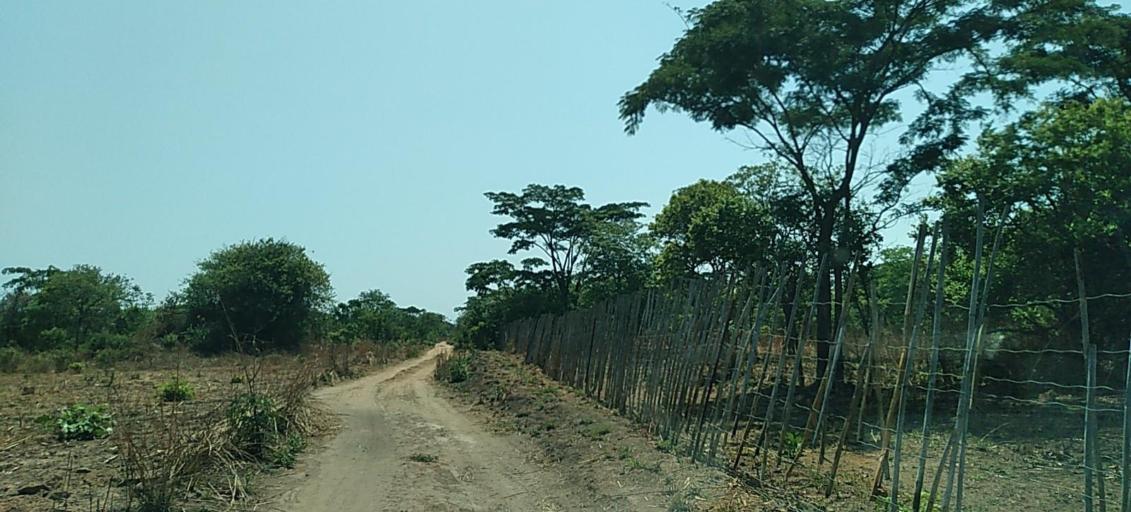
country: ZM
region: Copperbelt
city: Luanshya
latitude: -13.0082
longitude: 28.4718
